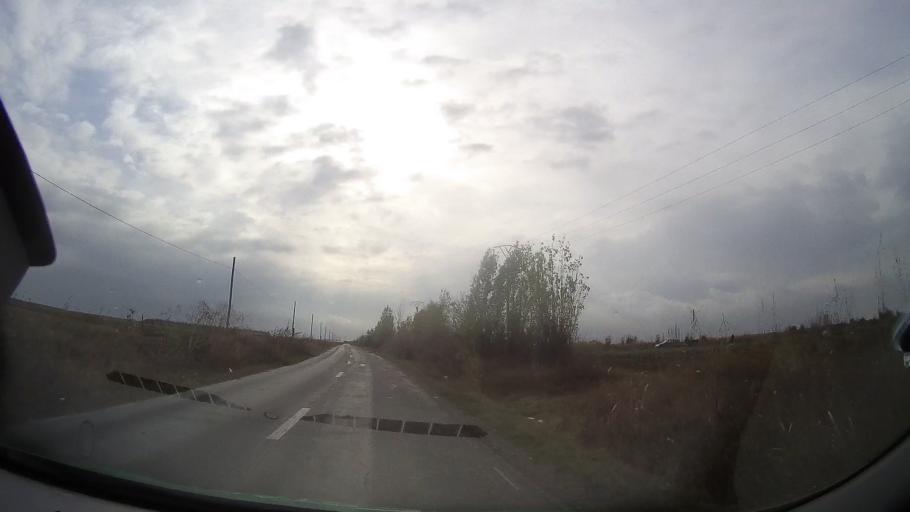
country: RO
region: Ialomita
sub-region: Comuna Maia
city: Maia
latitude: 44.7239
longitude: 26.3917
